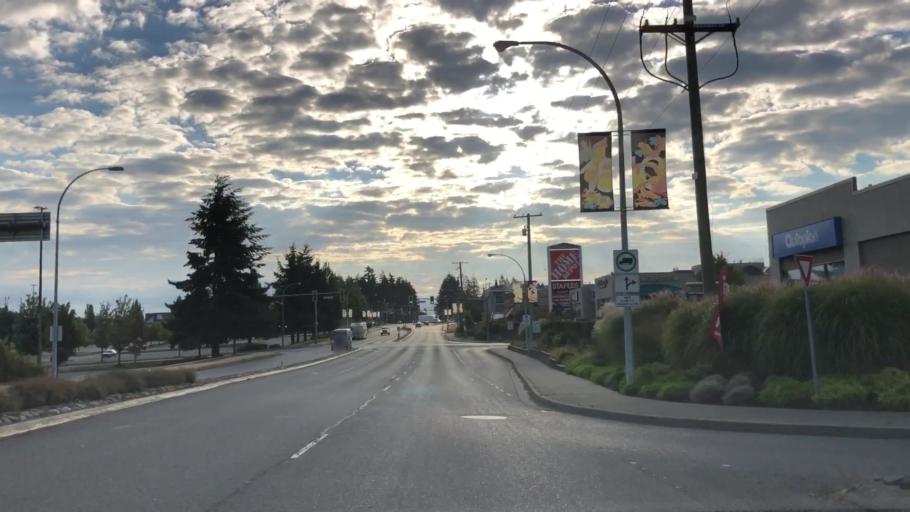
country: CA
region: British Columbia
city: Nanaimo
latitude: 49.2344
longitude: -124.0499
